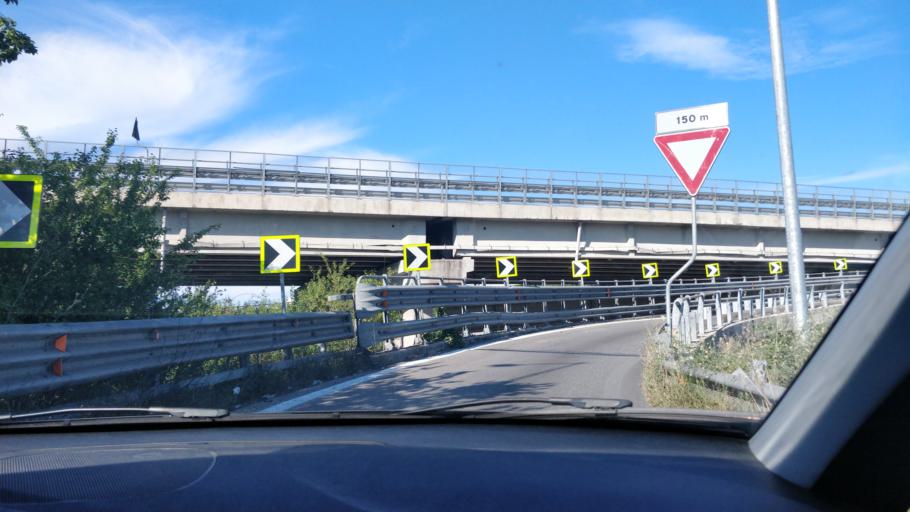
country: IT
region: Abruzzo
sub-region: Provincia di Pescara
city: Villa Raspa
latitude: 42.4447
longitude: 14.1892
